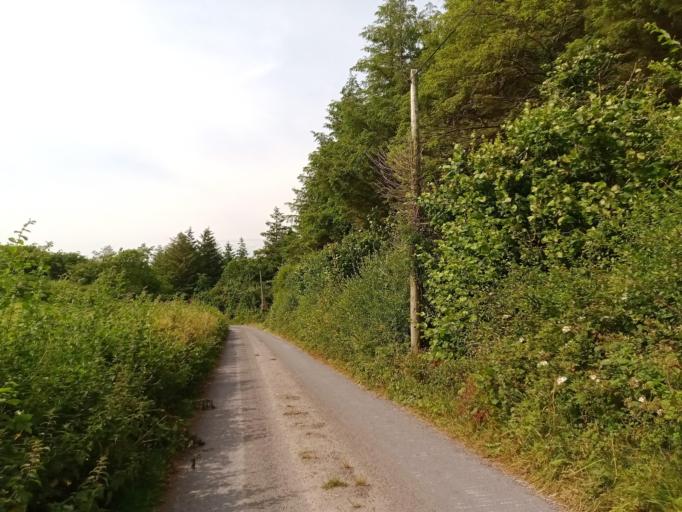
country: IE
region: Leinster
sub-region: Laois
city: Rathdowney
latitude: 52.8002
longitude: -7.4641
